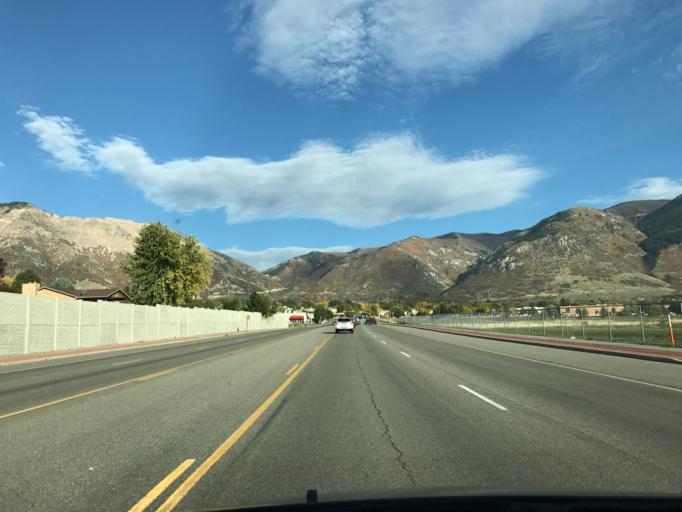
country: US
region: Utah
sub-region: Weber County
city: North Ogden
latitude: 41.3058
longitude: -111.9746
